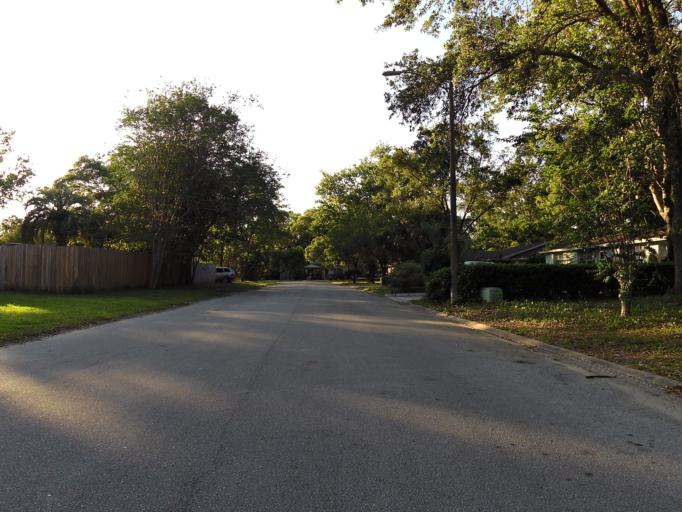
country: US
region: Florida
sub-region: Duval County
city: Jacksonville
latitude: 30.2409
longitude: -81.6041
